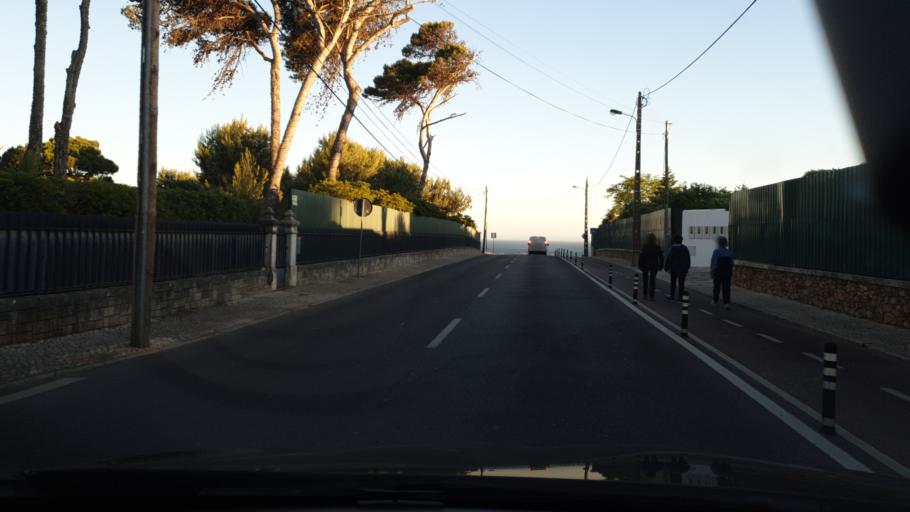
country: PT
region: Lisbon
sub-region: Cascais
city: Cascais
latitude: 38.6931
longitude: -9.4309
